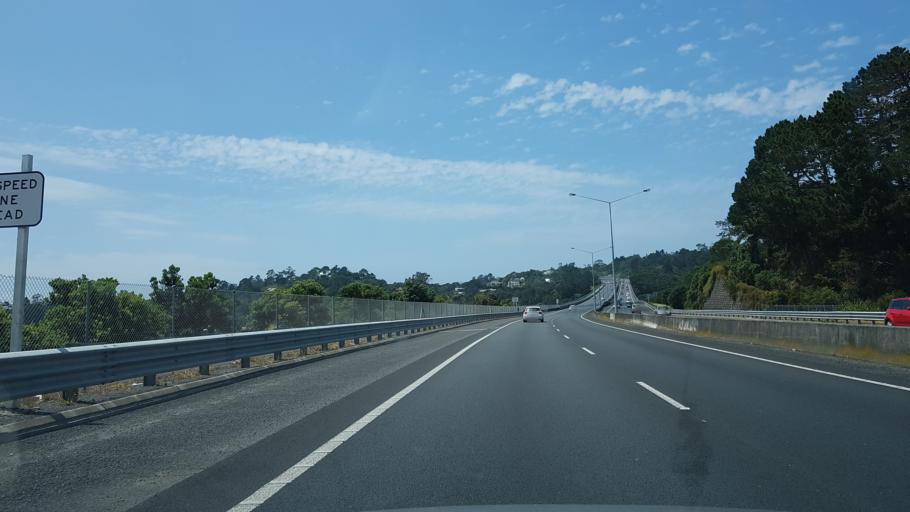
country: NZ
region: Auckland
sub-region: Auckland
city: Rosebank
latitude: -36.7865
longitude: 174.6621
